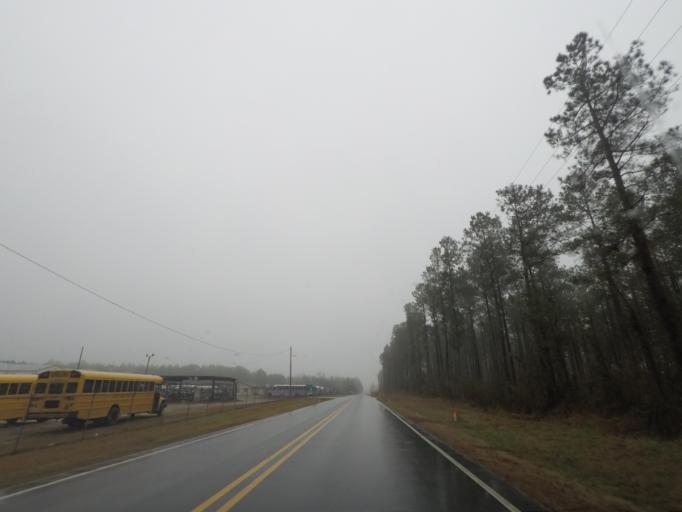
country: US
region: North Carolina
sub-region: Scotland County
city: Laurinburg
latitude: 34.8225
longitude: -79.4581
